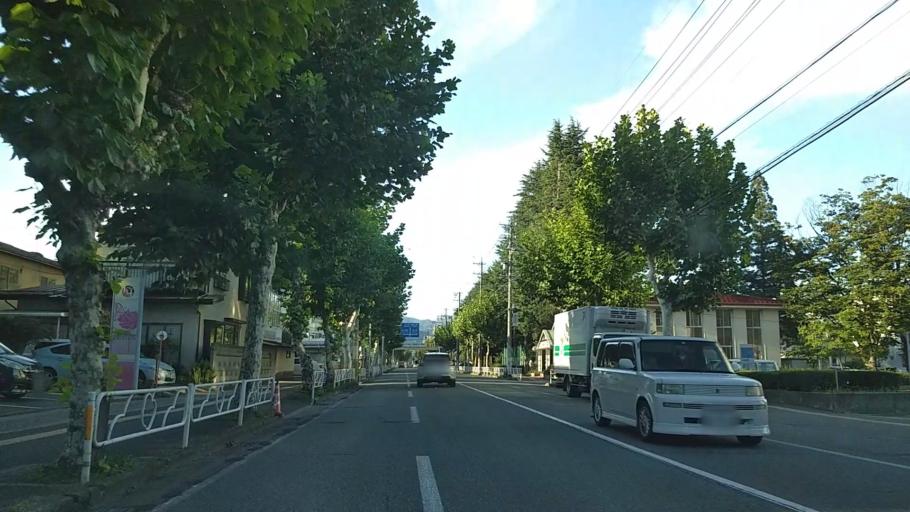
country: JP
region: Nagano
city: Nagano-shi
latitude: 36.6395
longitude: 138.1993
